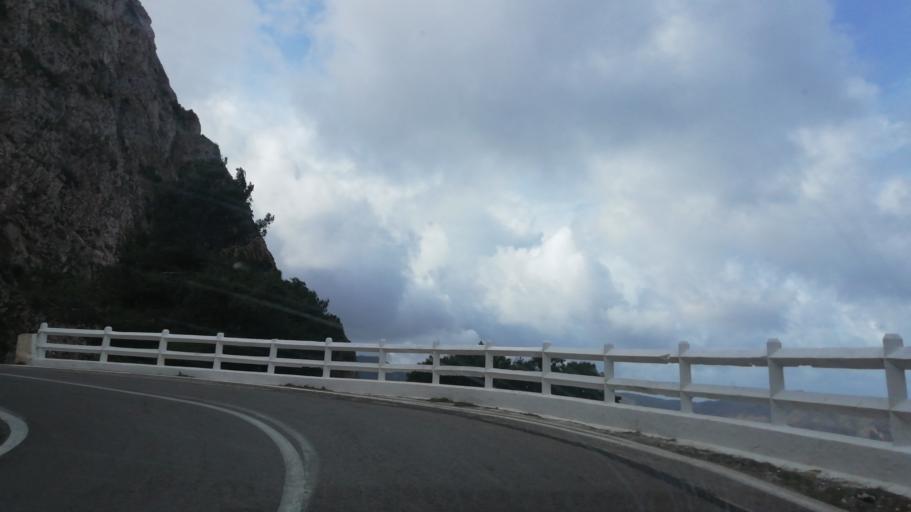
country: DZ
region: Oran
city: Oran
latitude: 35.7093
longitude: -0.6695
